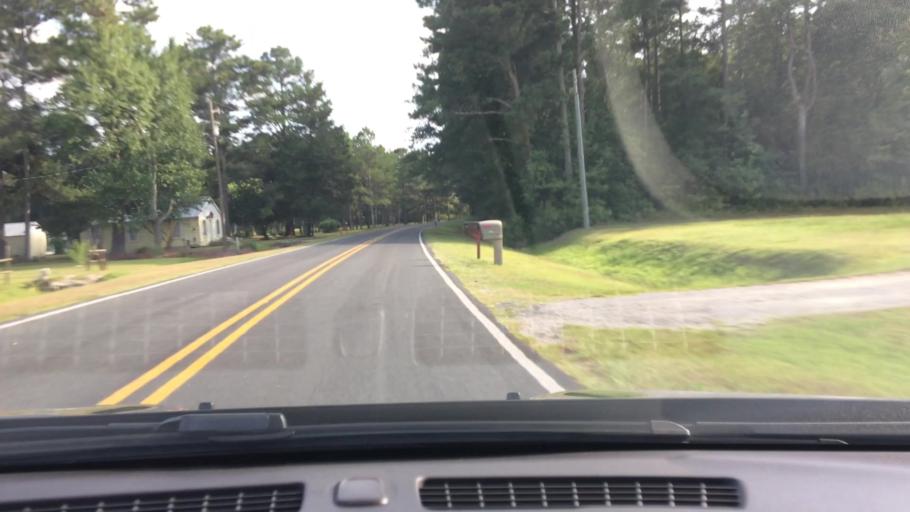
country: US
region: North Carolina
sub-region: Craven County
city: Vanceboro
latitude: 35.4349
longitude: -77.1242
